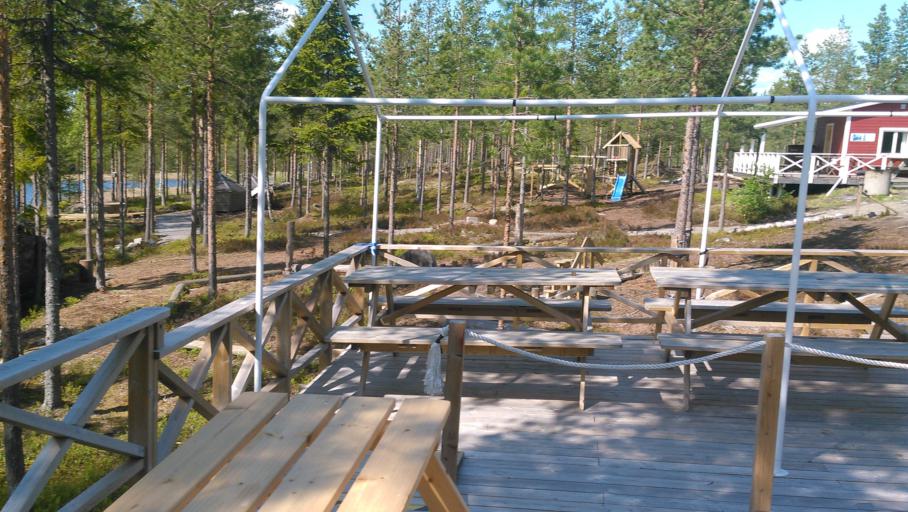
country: SE
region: Vaesterbotten
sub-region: Vannas Kommun
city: Vannasby
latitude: 63.8234
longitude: 19.9044
